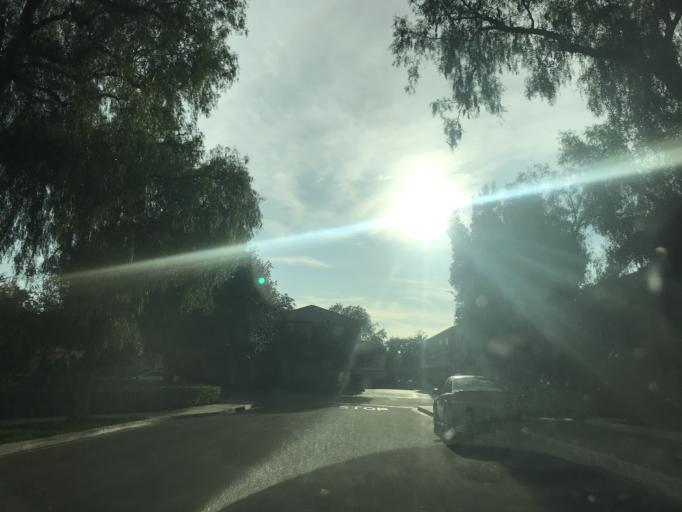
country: US
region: California
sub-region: Orange County
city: Lake Forest
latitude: 33.6986
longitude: -117.7472
